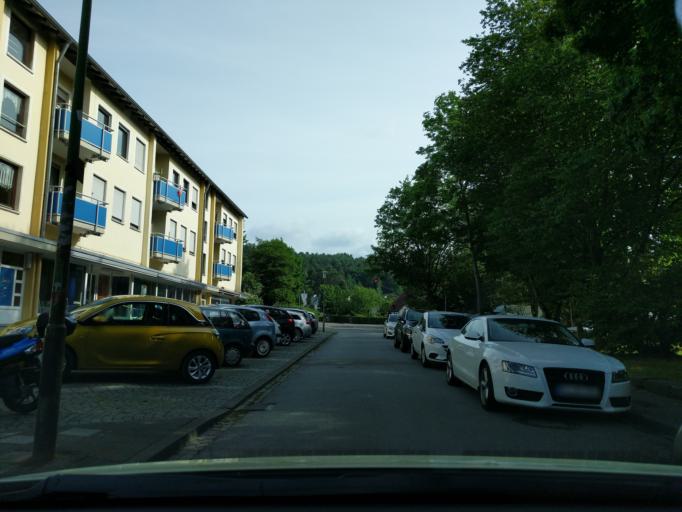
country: DE
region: Rheinland-Pfalz
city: Kaiserslautern
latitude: 49.4394
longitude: 7.7335
